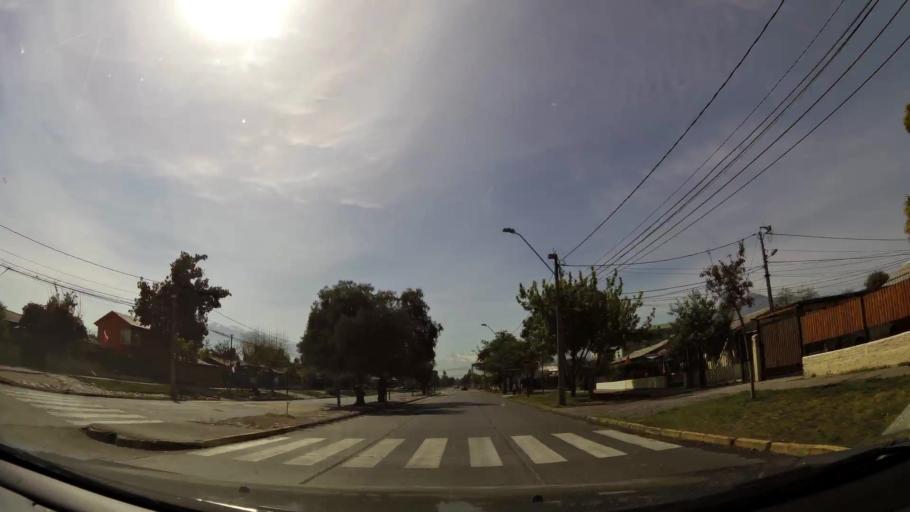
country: CL
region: Santiago Metropolitan
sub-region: Provincia de Cordillera
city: Puente Alto
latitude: -33.6184
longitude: -70.5889
